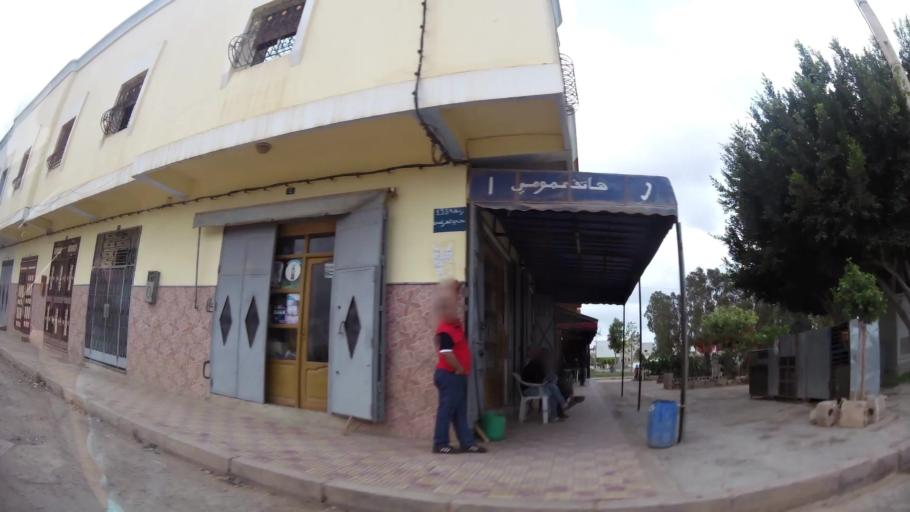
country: MA
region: Oriental
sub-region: Nador
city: Nador
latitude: 35.1602
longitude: -2.9164
